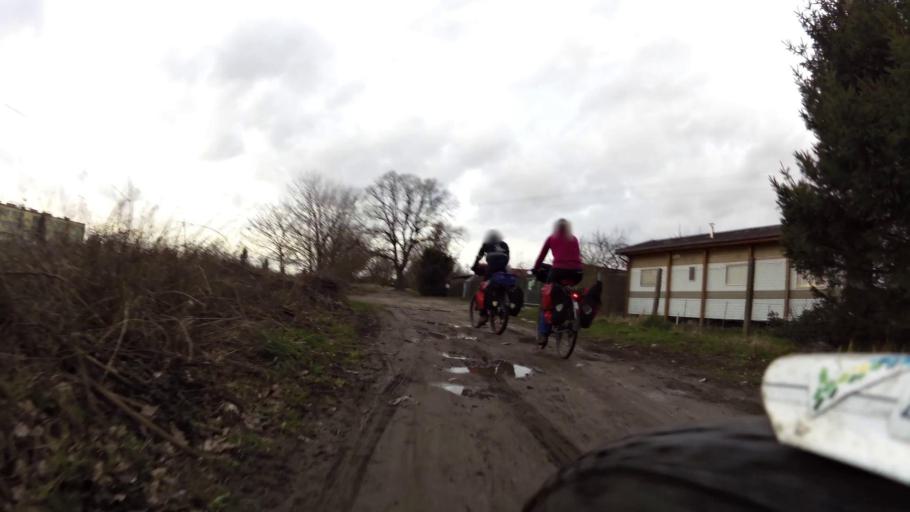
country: PL
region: West Pomeranian Voivodeship
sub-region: Powiat kamienski
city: Kamien Pomorski
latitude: 53.9517
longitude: 14.7724
